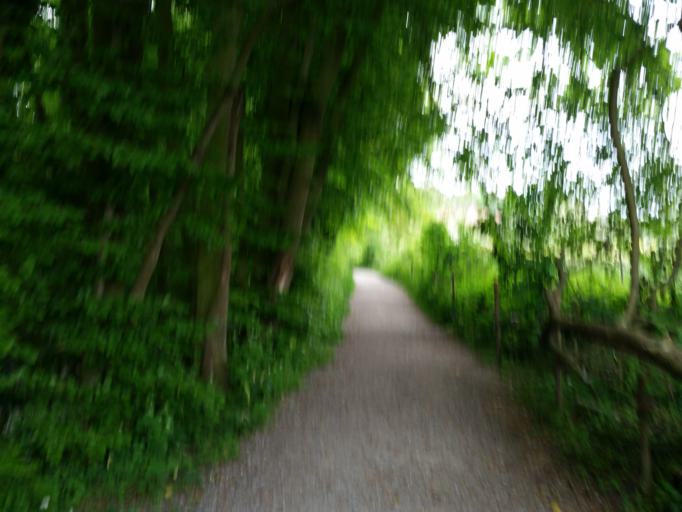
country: CH
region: Thurgau
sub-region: Kreuzlingen District
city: Guttingen
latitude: 47.6064
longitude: 9.3053
